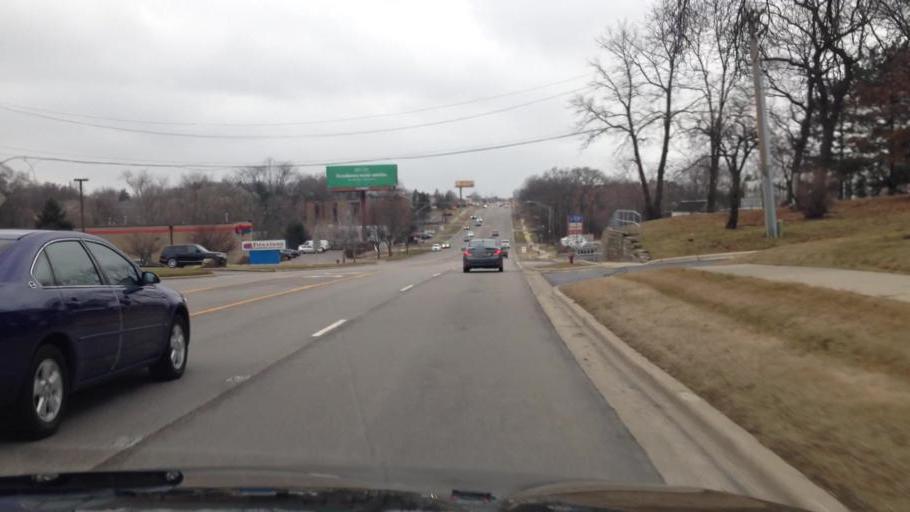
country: US
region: Illinois
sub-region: DuPage County
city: Lisle
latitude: 41.7966
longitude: -88.1076
